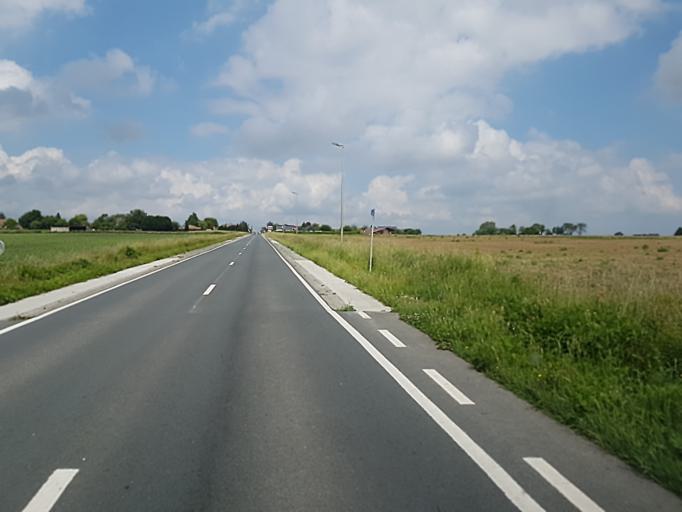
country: BE
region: Wallonia
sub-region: Province du Brabant Wallon
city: Rebecq-Rognon
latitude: 50.6884
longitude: 4.1283
